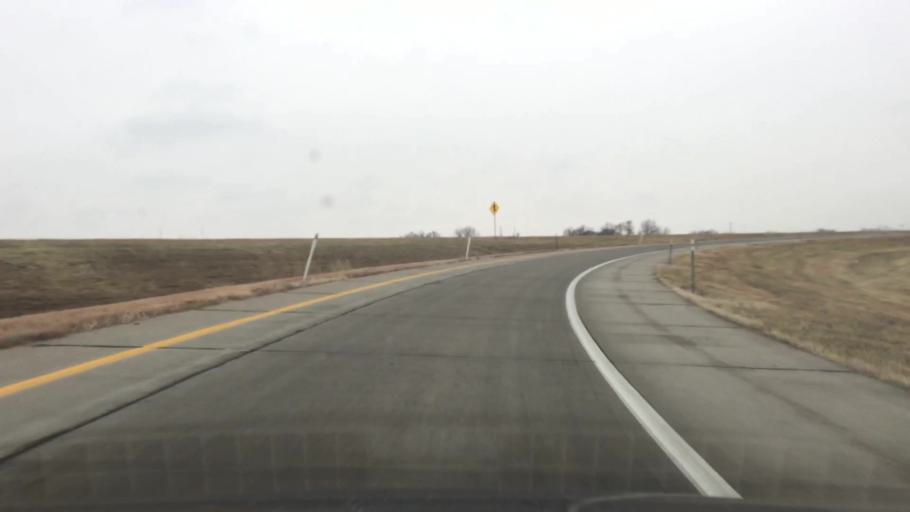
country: US
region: Kansas
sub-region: Shawnee County
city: Topeka
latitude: 39.0330
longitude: -95.6122
